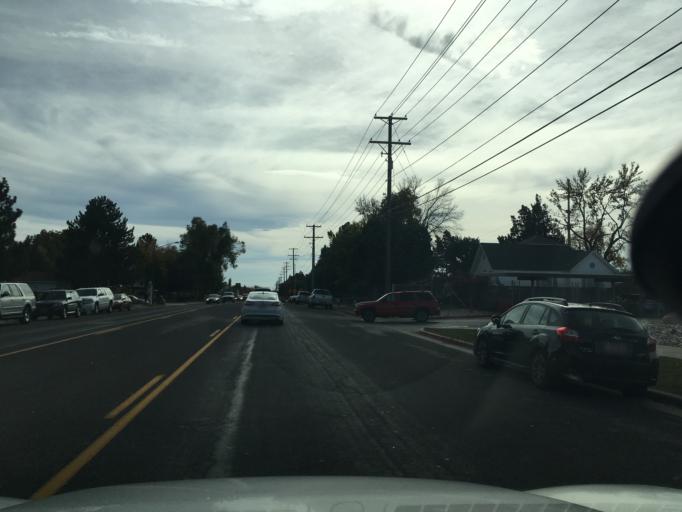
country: US
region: Utah
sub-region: Davis County
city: Layton
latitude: 41.0648
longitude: -111.9576
